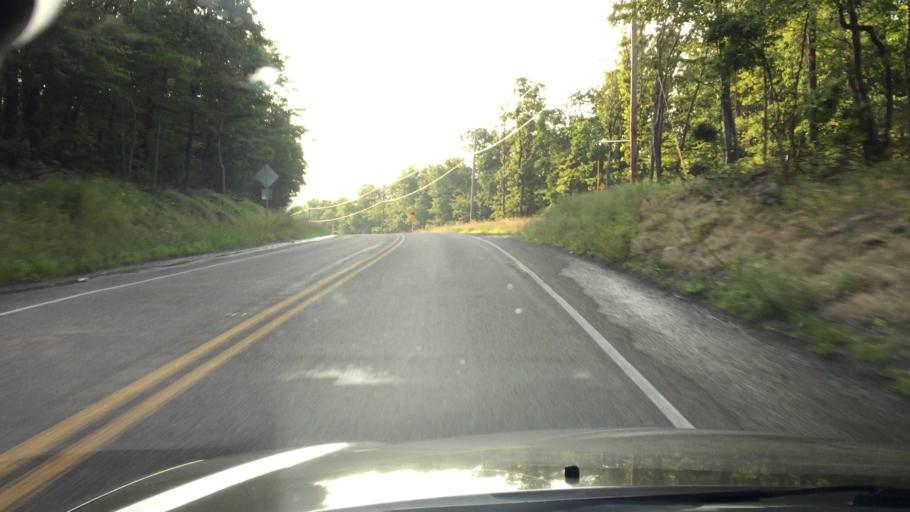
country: US
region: Pennsylvania
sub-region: Carbon County
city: Weatherly
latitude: 40.9265
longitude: -75.8918
